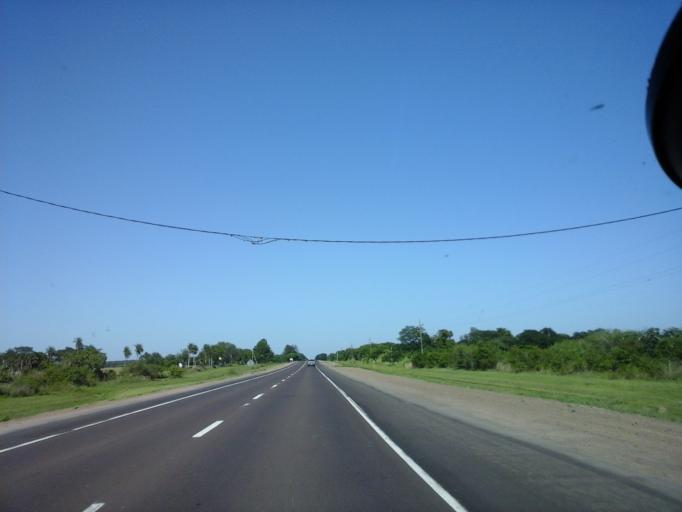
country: AR
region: Corrientes
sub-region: Departamento de San Cosme
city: San Cosme
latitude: -27.3676
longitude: -58.3783
